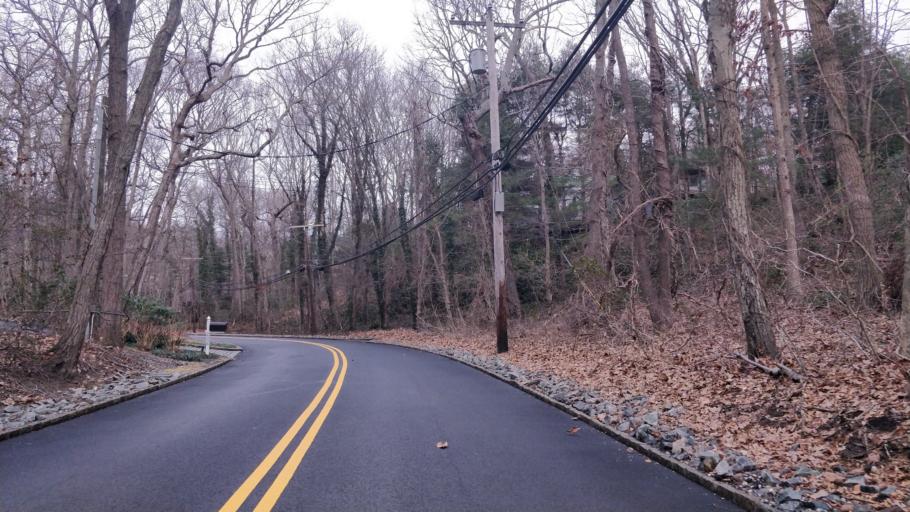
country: US
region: New York
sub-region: Nassau County
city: Laurel Hollow
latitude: 40.8642
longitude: -73.4834
